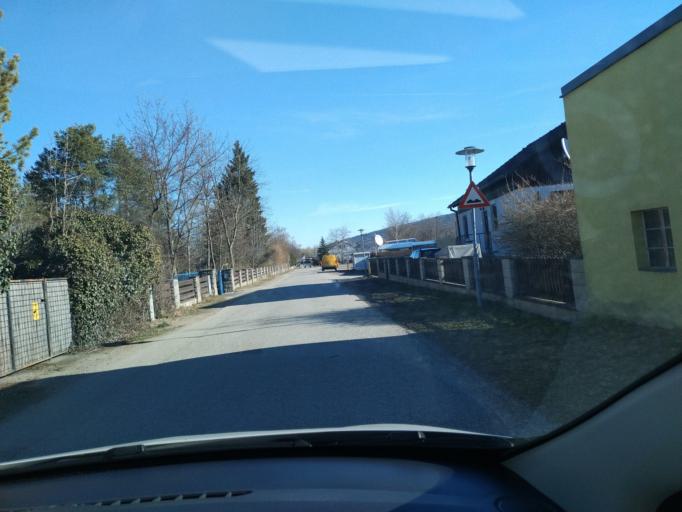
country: AT
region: Lower Austria
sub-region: Politischer Bezirk Wiener Neustadt
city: Lanzenkirchen
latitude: 47.7486
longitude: 16.2530
